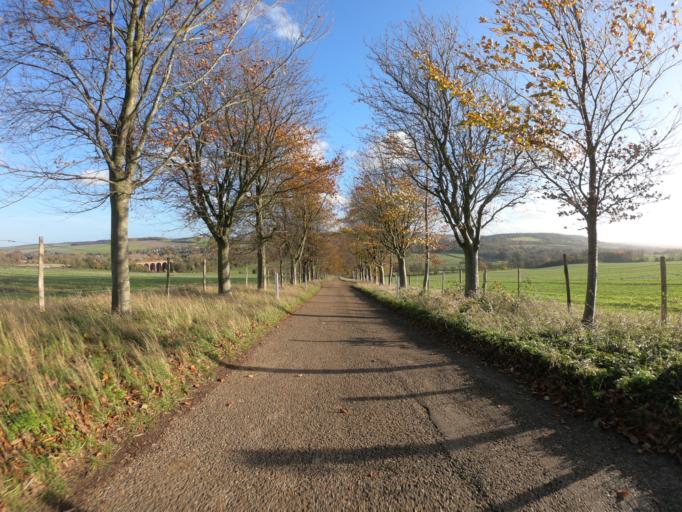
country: GB
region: England
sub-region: Kent
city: Eynsford
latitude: 51.3692
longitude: 0.1955
